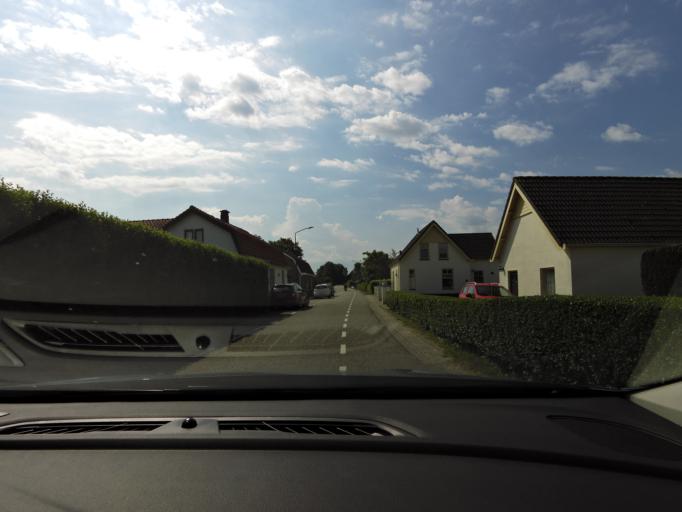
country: NL
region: North Brabant
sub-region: Gemeente Woudrichem
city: Almkerk
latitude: 51.7960
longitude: 4.9381
